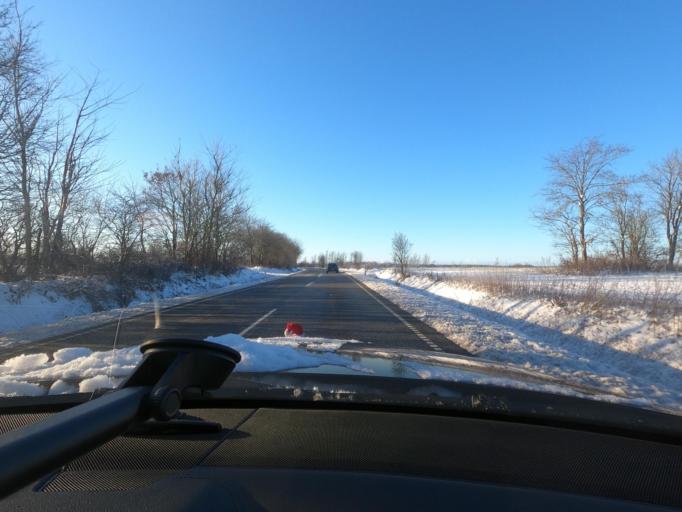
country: DK
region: South Denmark
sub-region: Tonder Kommune
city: Toftlund
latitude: 55.1779
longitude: 9.0059
